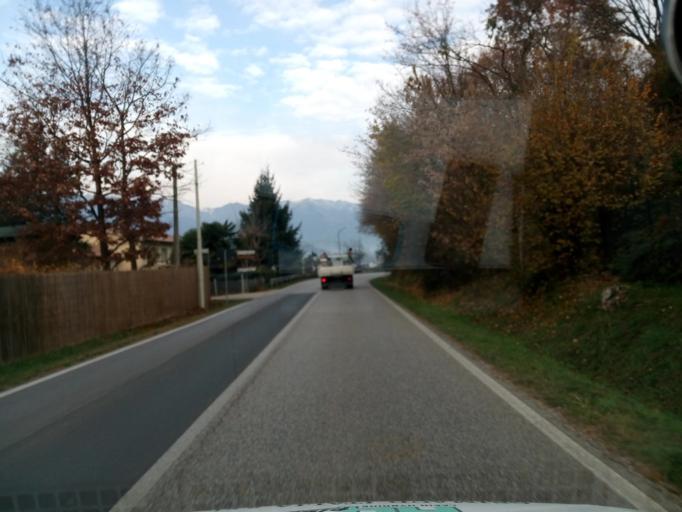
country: IT
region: Veneto
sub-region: Provincia di Treviso
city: Villa d'Asolo
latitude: 45.7917
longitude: 11.8968
